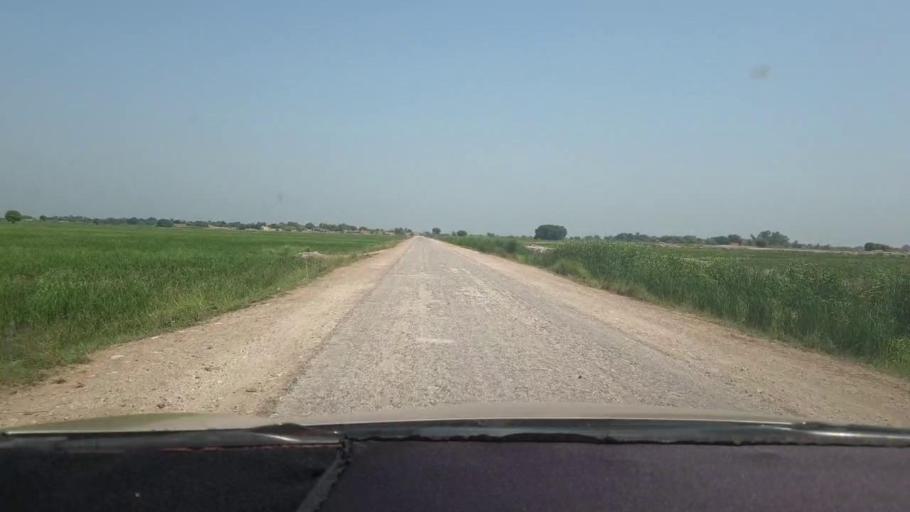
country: PK
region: Sindh
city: Miro Khan
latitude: 27.6875
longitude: 68.0859
